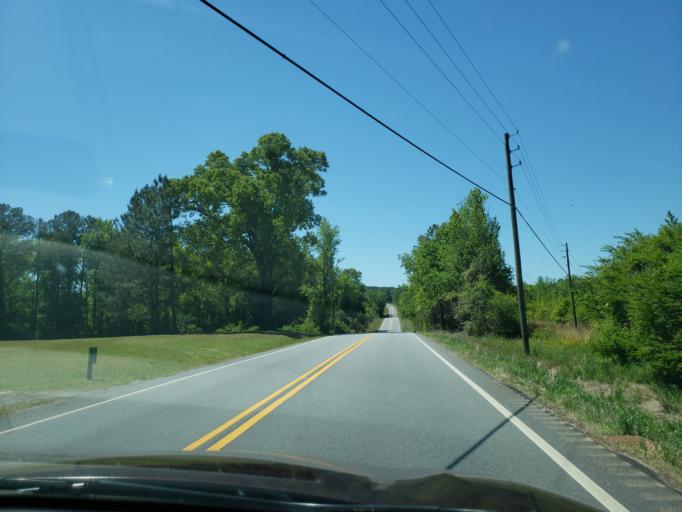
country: US
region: Alabama
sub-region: Tallapoosa County
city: Dadeville
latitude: 32.6815
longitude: -85.7880
